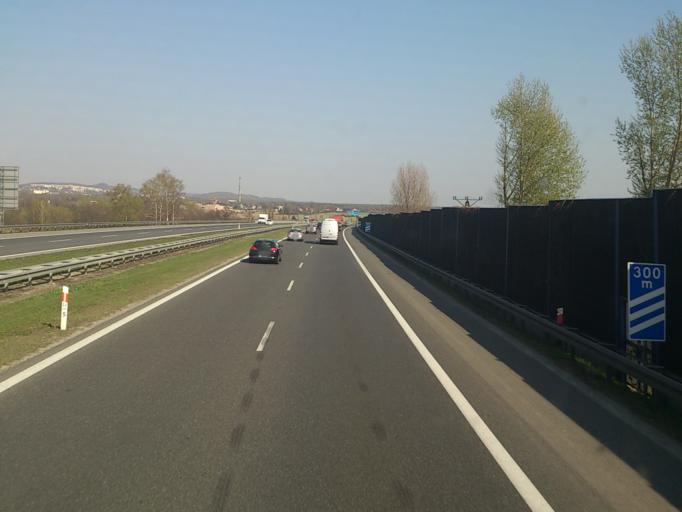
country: PL
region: Lesser Poland Voivodeship
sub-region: Powiat chrzanowski
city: Chrzanow
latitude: 50.1507
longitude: 19.4130
